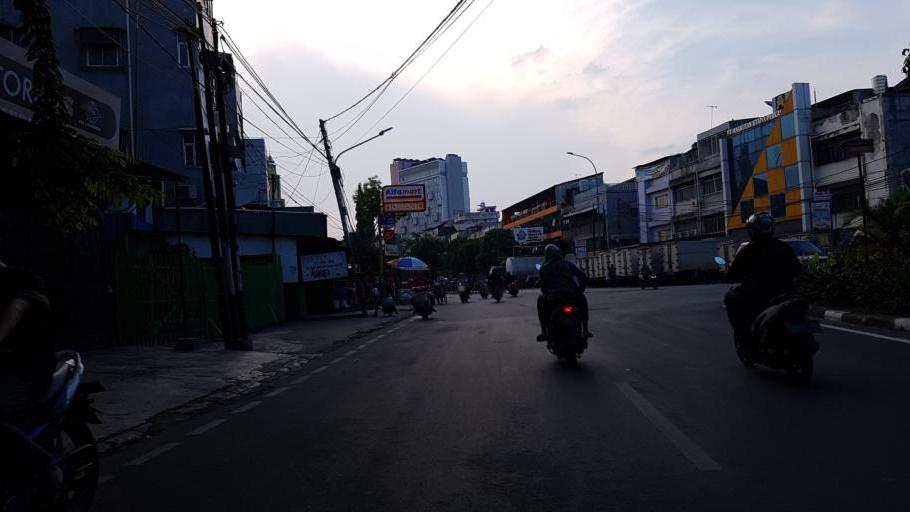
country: ID
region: Jakarta Raya
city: Jakarta
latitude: -6.1374
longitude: 106.7912
